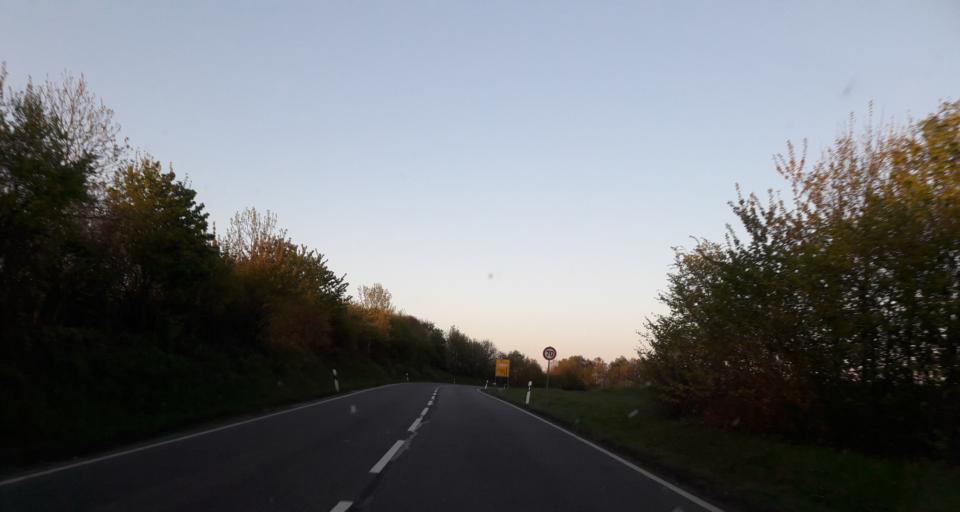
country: DE
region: Rheinland-Pfalz
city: Monzelfeld
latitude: 49.8863
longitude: 7.0816
